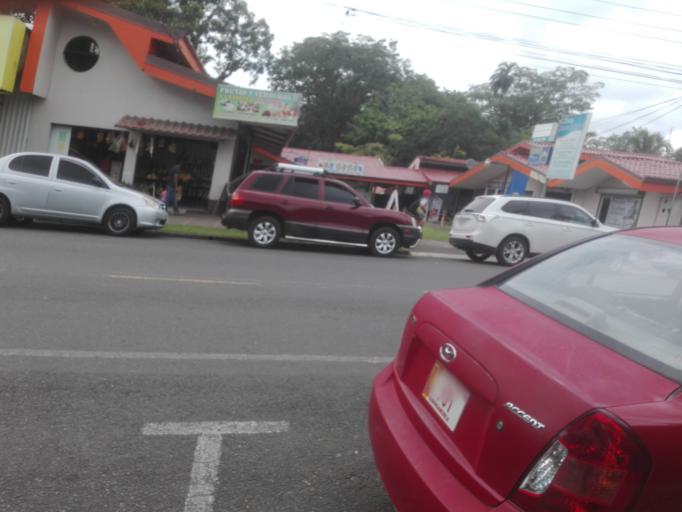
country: CR
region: Heredia
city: La Virgen
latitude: 10.4559
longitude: -84.0081
